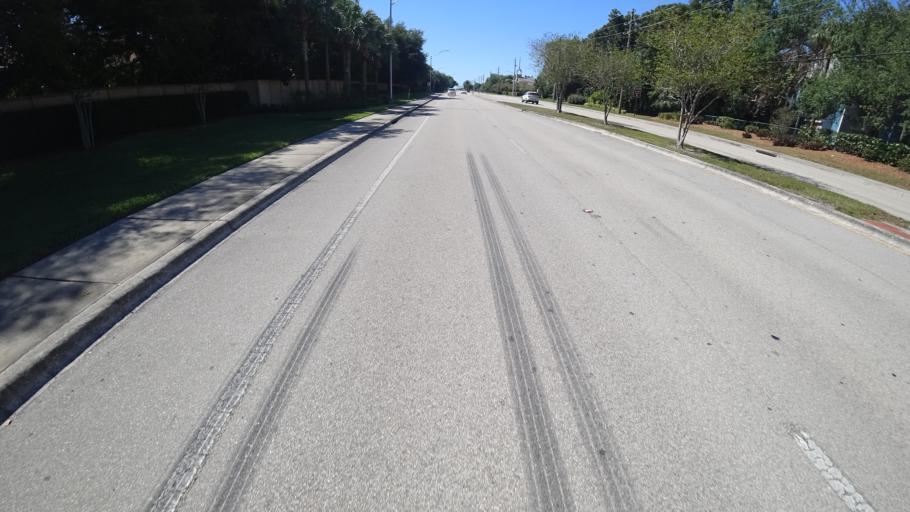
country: US
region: Florida
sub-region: Manatee County
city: West Bradenton
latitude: 27.4674
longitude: -82.6368
